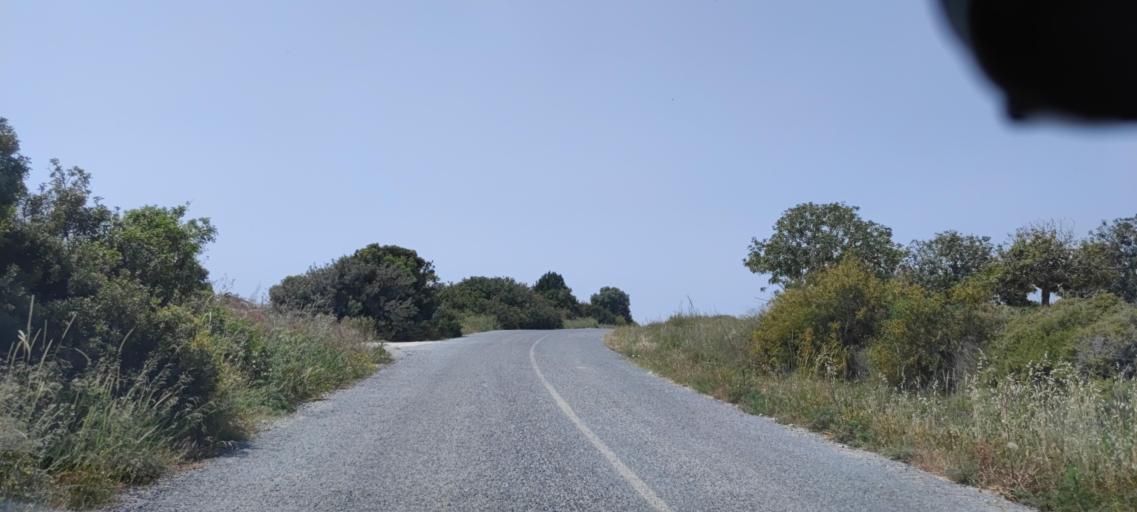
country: CY
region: Ammochostos
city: Rizokarpaso
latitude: 35.5220
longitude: 34.3198
